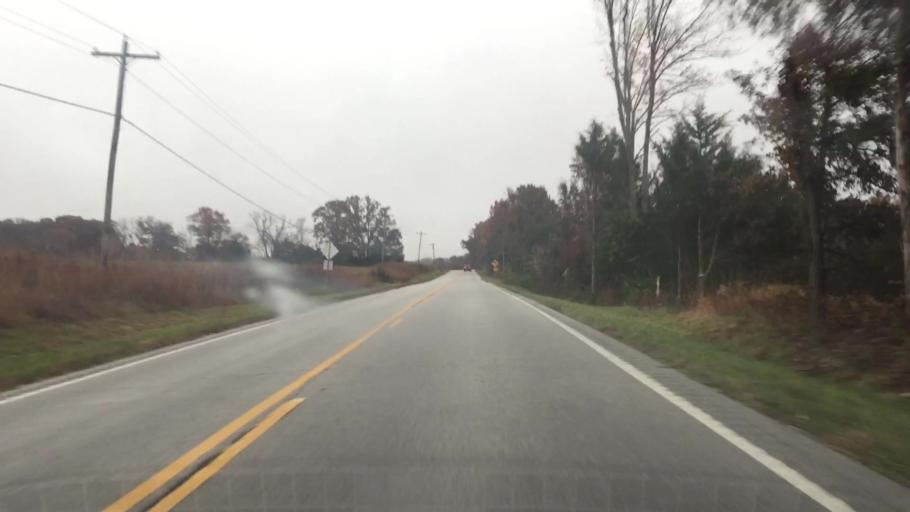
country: US
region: Missouri
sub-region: Callaway County
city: Fulton
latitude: 38.8865
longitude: -92.0961
